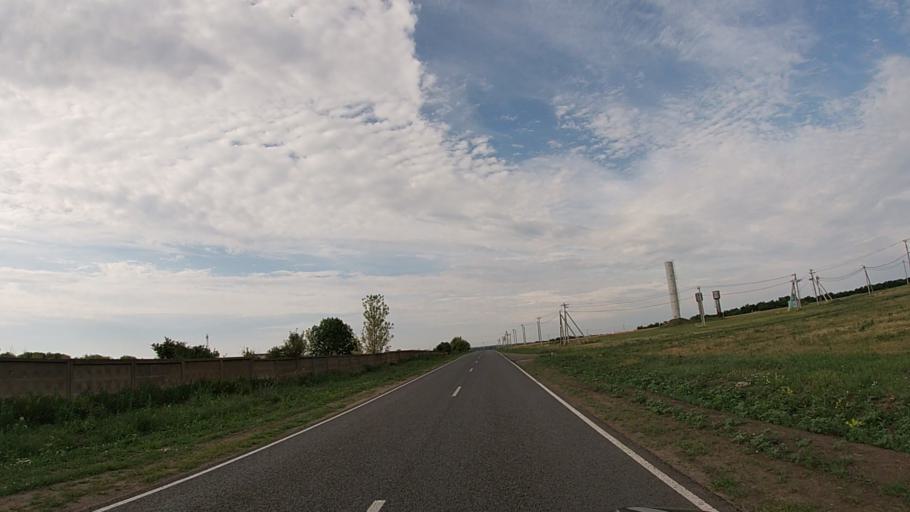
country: RU
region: Belgorod
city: Severnyy
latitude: 50.7249
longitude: 36.5844
